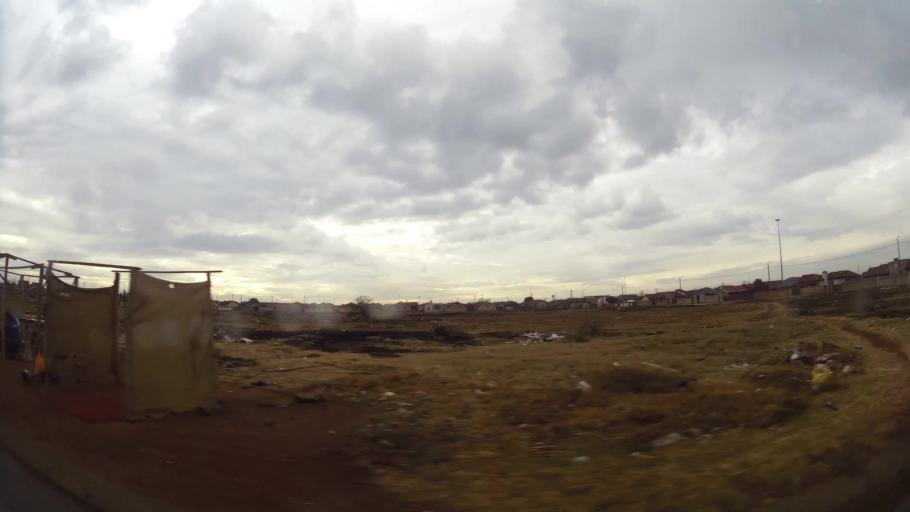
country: ZA
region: Gauteng
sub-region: Ekurhuleni Metropolitan Municipality
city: Germiston
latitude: -26.3340
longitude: 28.2047
